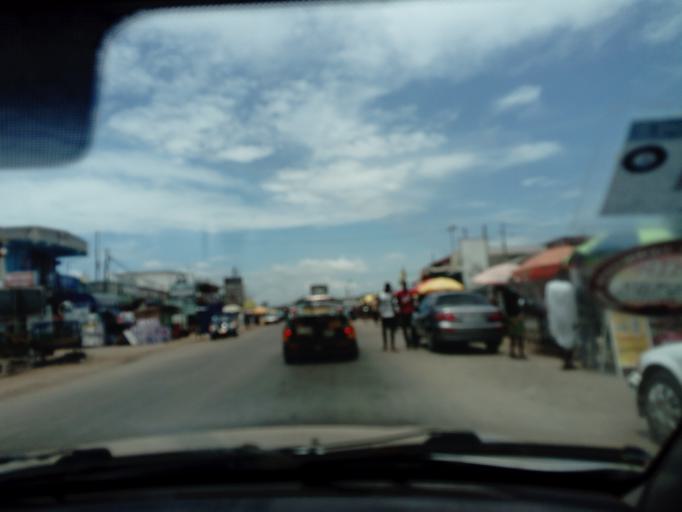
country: GH
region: Central
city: Cape Coast
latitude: 5.1316
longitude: -1.2755
